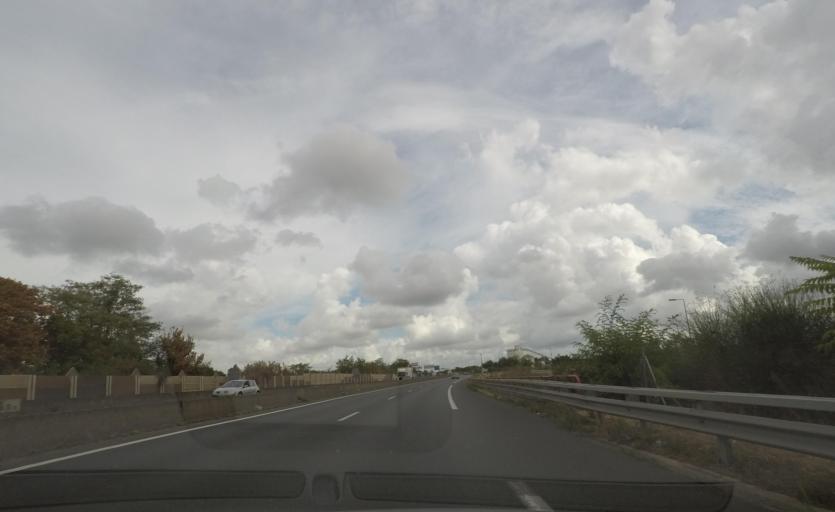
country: FR
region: Pays de la Loire
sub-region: Departement de Maine-et-Loire
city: Angers
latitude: 47.4600
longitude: -0.5178
